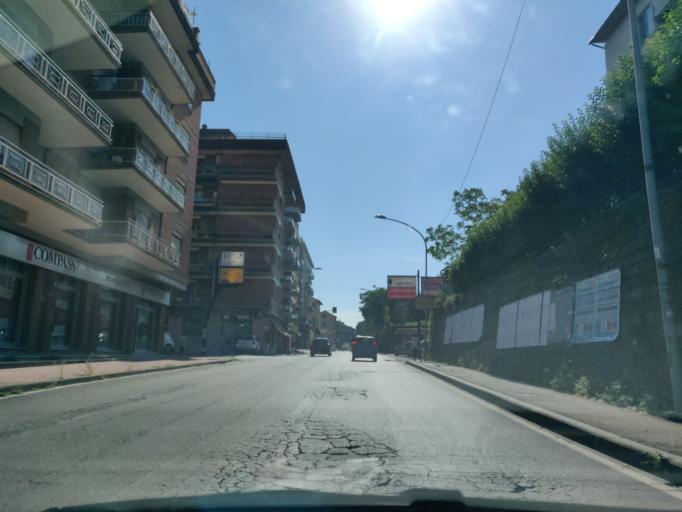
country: IT
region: Latium
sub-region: Provincia di Viterbo
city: Viterbo
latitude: 42.4248
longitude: 12.1001
